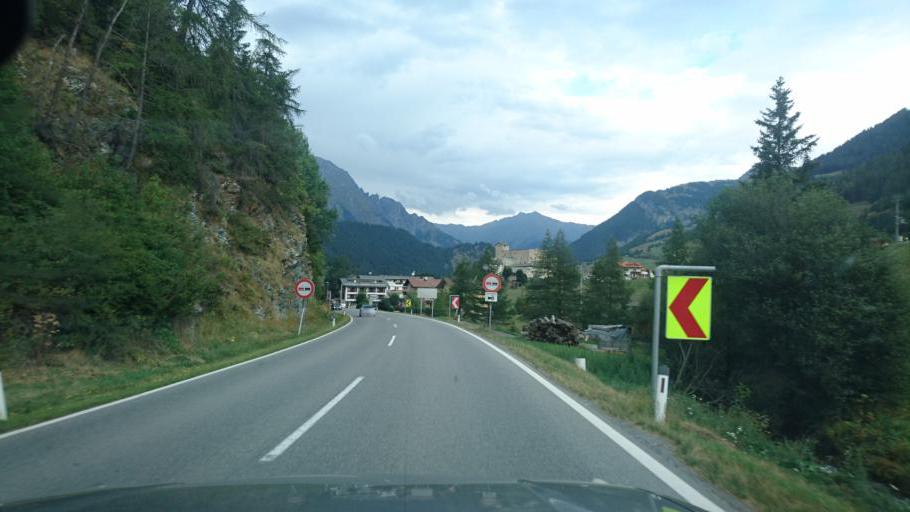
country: AT
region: Tyrol
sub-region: Politischer Bezirk Landeck
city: Nauders
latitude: 46.8834
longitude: 10.5049
